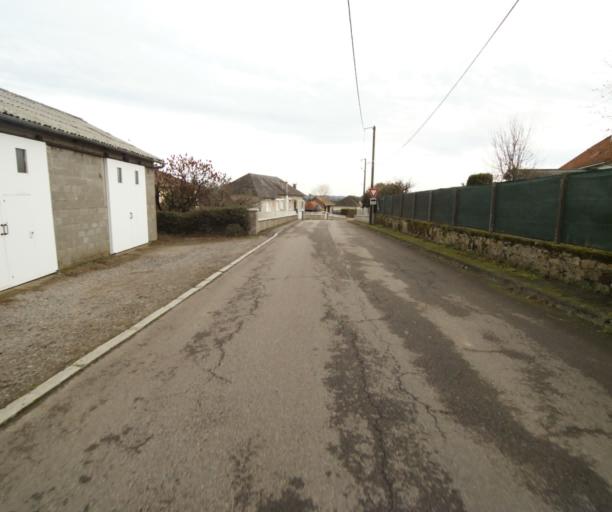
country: FR
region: Limousin
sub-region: Departement de la Correze
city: Chameyrat
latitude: 45.2661
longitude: 1.7210
